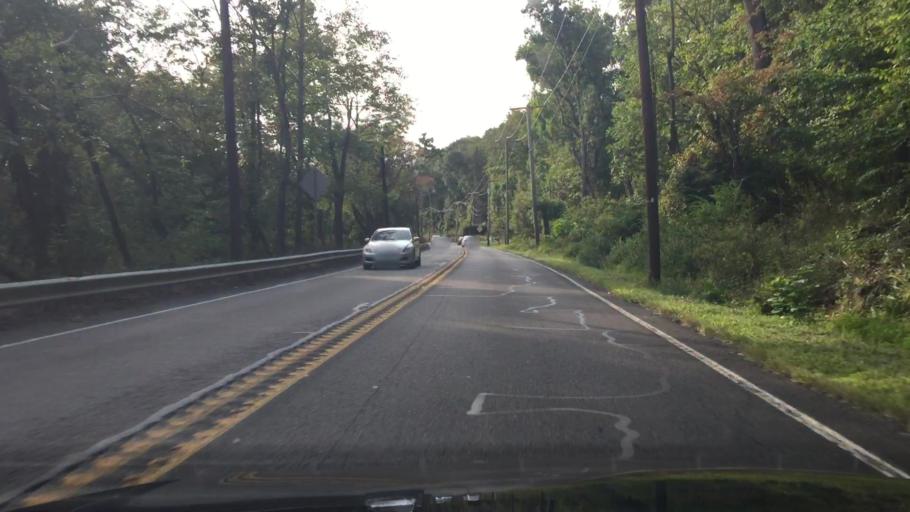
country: US
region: New Jersey
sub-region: Hunterdon County
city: Lambertville
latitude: 40.3163
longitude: -74.8954
